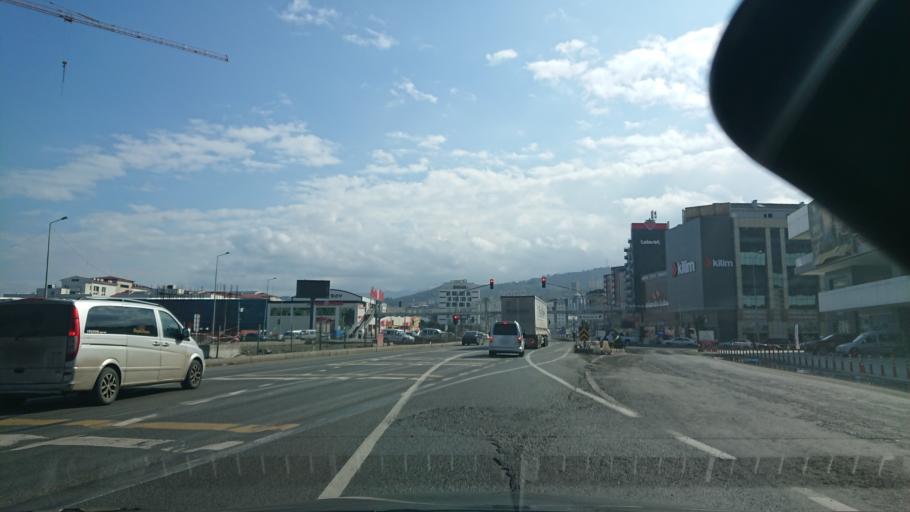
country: TR
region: Trabzon
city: Yomra
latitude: 40.9681
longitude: 39.8352
